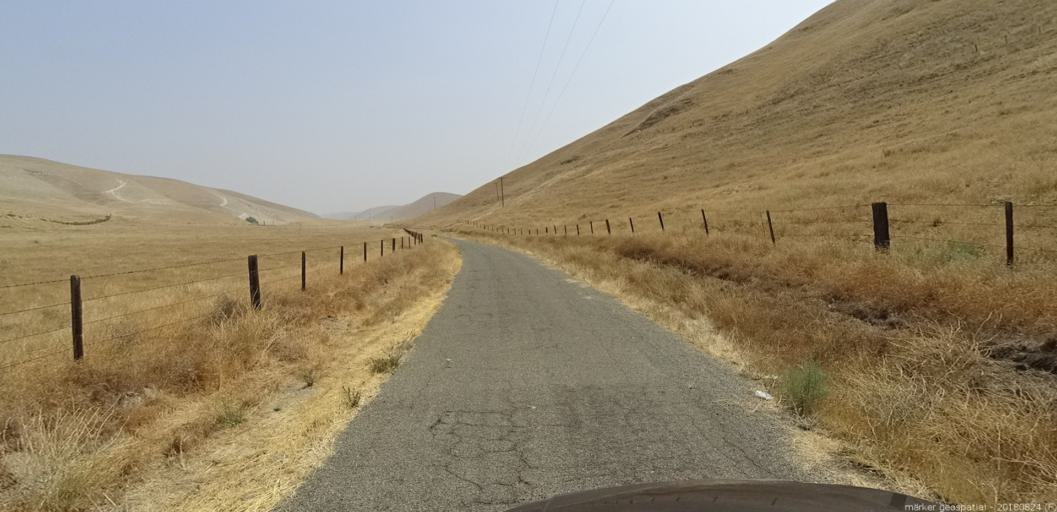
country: US
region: California
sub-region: Monterey County
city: King City
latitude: 36.1917
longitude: -120.9904
